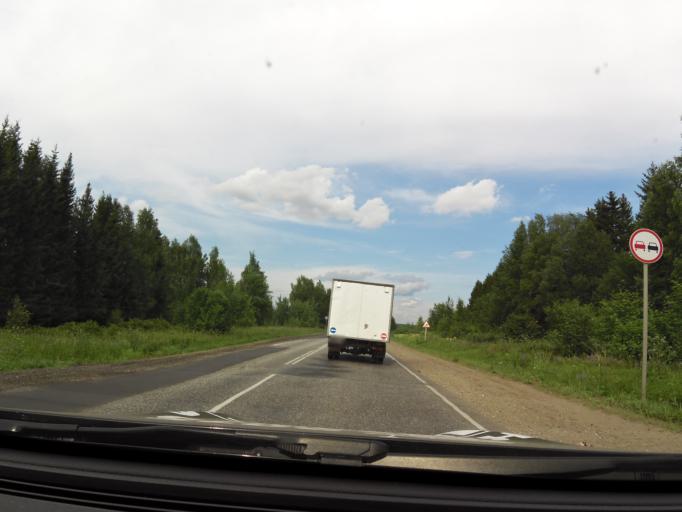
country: RU
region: Kirov
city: Stulovo
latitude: 58.7051
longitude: 50.0957
